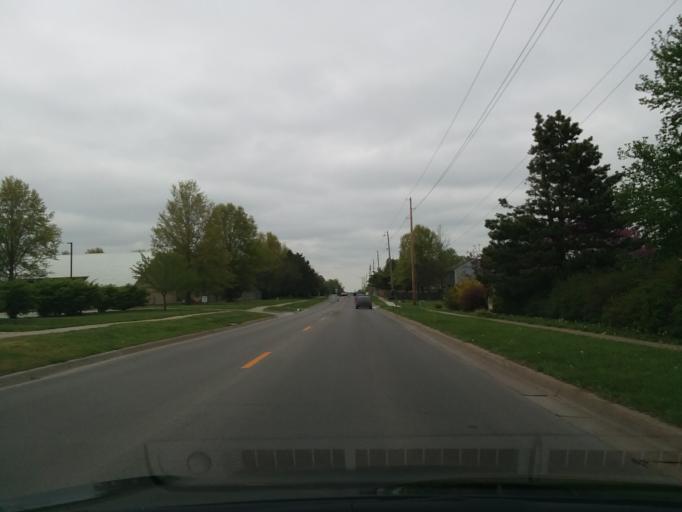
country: US
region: Kansas
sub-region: Douglas County
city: Lawrence
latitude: 38.9744
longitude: -95.2883
